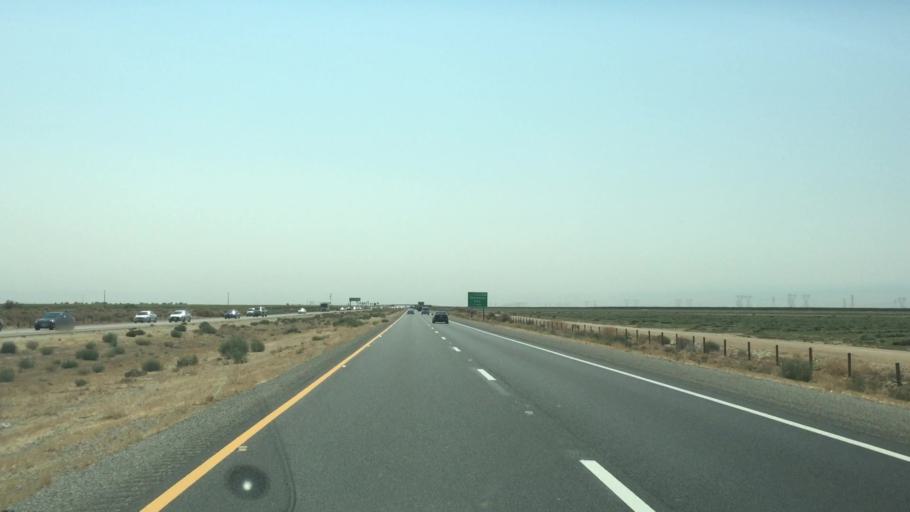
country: US
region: California
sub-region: Kern County
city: Buttonwillow
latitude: 35.3691
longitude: -119.3562
